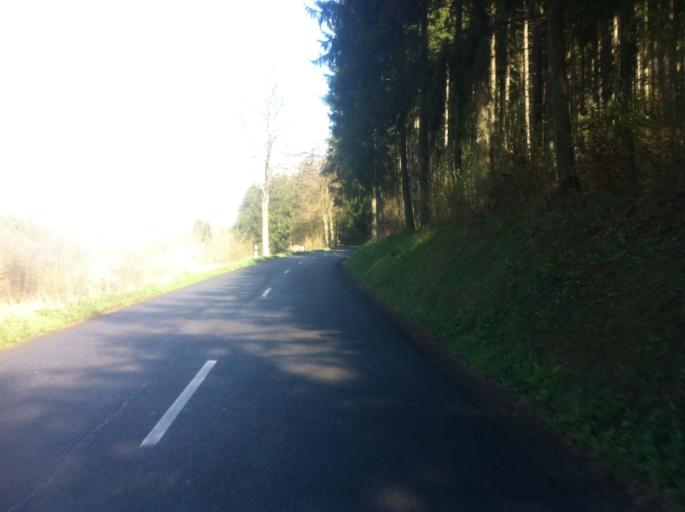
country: LU
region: Diekirch
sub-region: Canton de Wiltz
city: Wilwerwiltz
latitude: 50.0162
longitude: 6.0107
